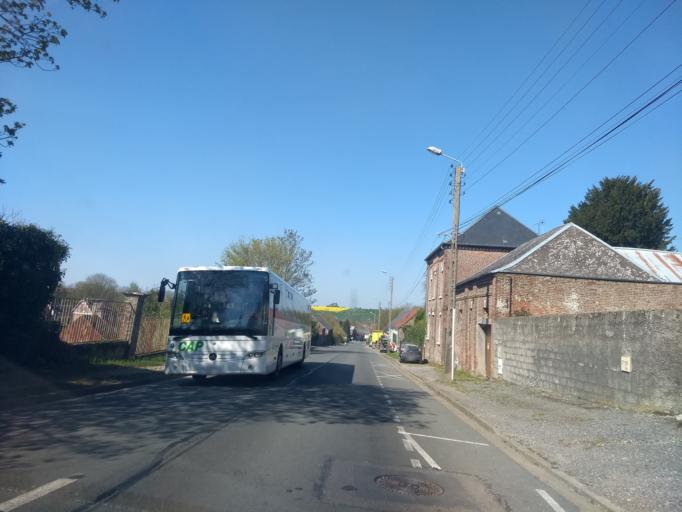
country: FR
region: Picardie
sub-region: Departement de la Somme
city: Beauval
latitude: 50.1078
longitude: 2.3349
